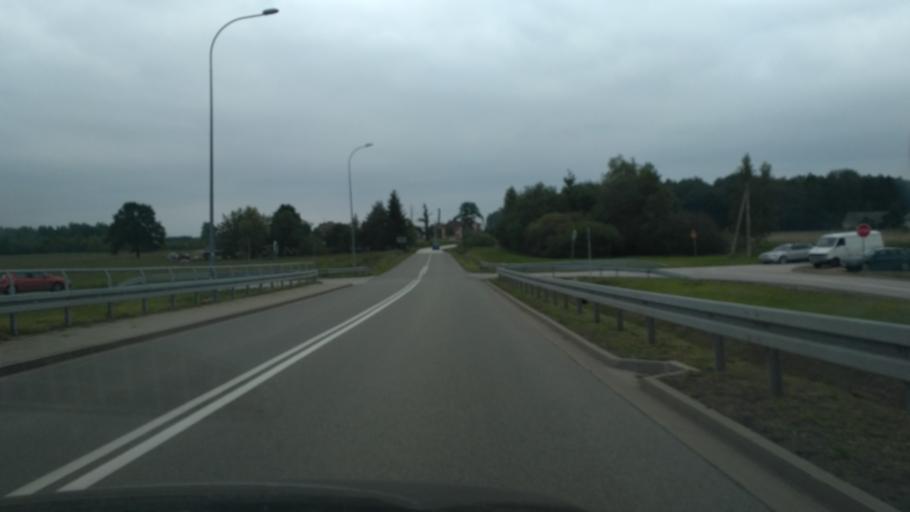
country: PL
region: Subcarpathian Voivodeship
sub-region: Powiat ropczycko-sedziszowski
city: Sedziszow Malopolski
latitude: 50.1099
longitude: 21.6717
